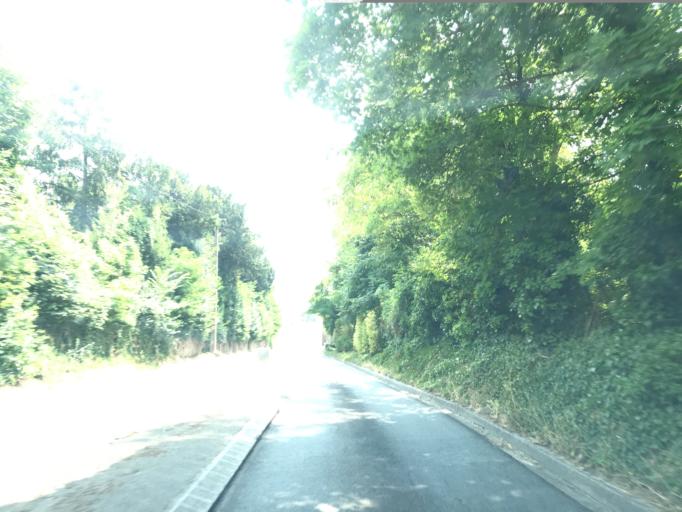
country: FR
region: Haute-Normandie
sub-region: Departement de l'Eure
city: Breuilpont
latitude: 48.9654
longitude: 1.4261
